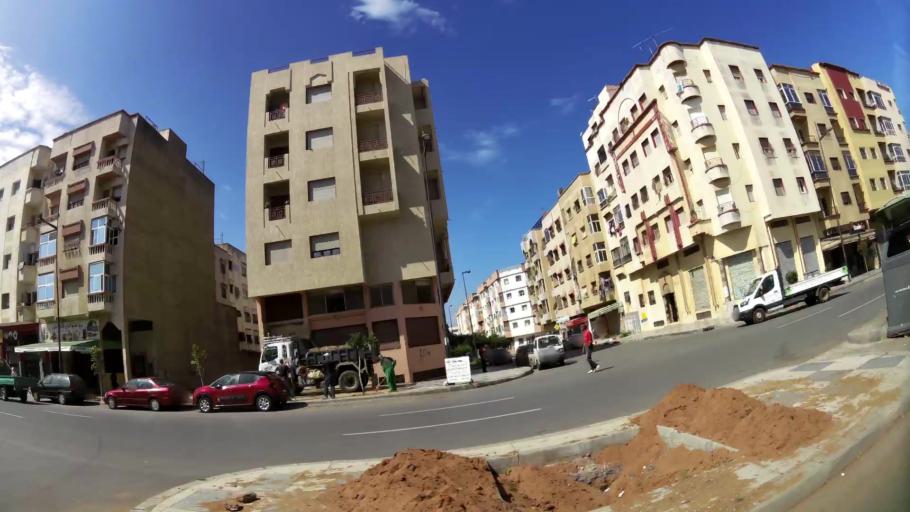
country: MA
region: Rabat-Sale-Zemmour-Zaer
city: Sale
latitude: 34.0697
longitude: -6.7927
